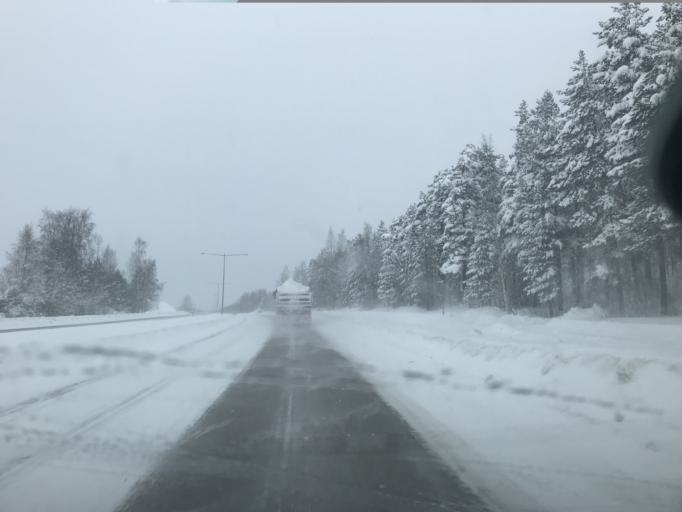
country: SE
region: Norrbotten
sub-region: Lulea Kommun
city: Lulea
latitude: 65.6070
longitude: 22.1383
